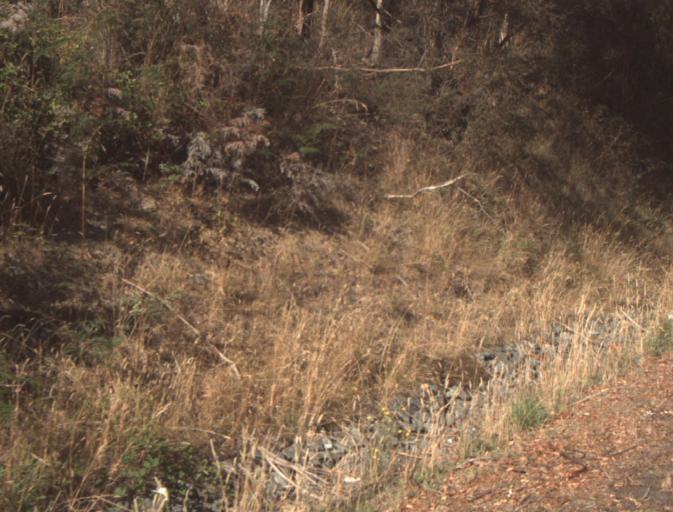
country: AU
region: Tasmania
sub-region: Dorset
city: Bridport
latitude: -41.1665
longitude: 147.2341
